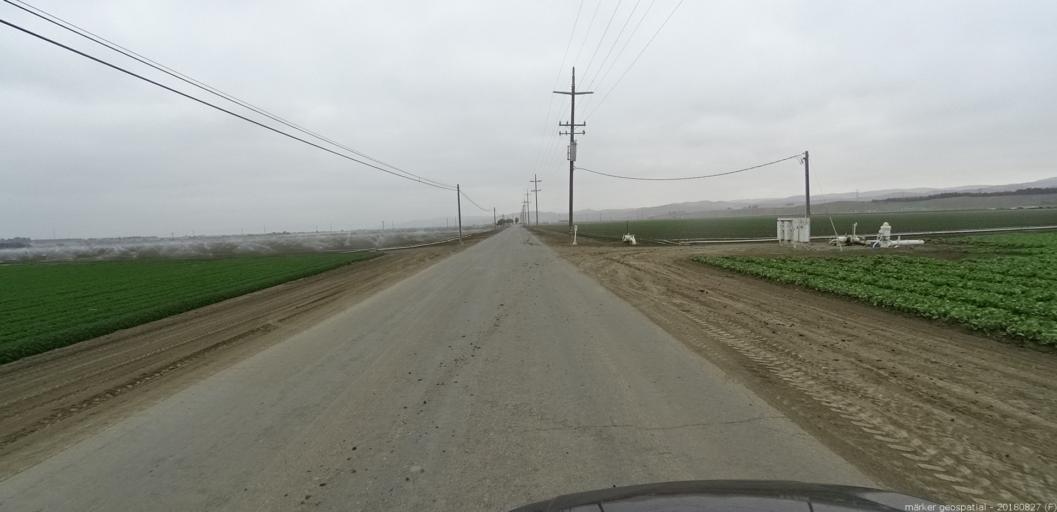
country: US
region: California
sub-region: Monterey County
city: King City
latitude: 36.2556
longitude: -121.1510
